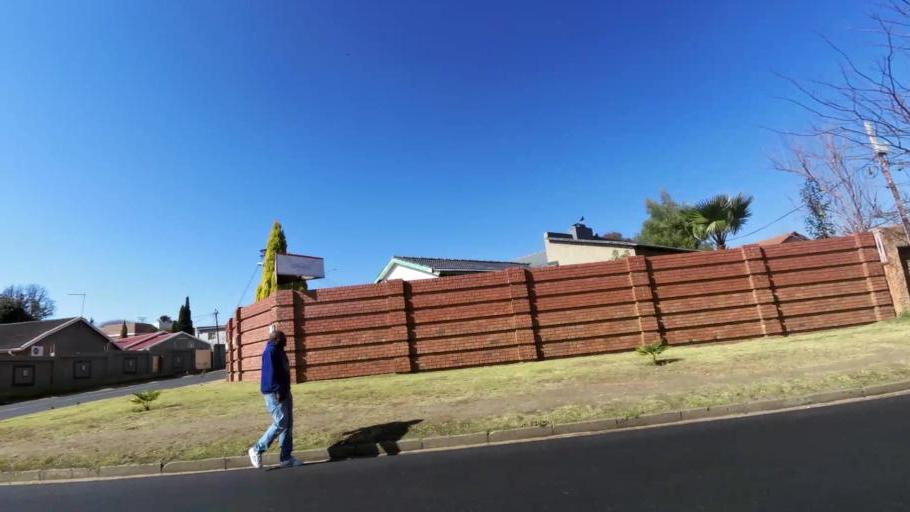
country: ZA
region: Gauteng
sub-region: City of Johannesburg Metropolitan Municipality
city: Johannesburg
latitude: -26.2468
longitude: 27.9995
